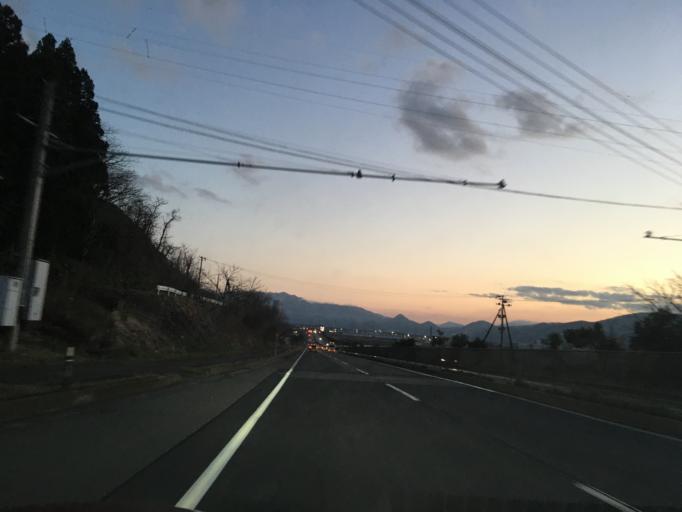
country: JP
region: Yamagata
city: Kaminoyama
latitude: 38.1610
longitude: 140.3015
